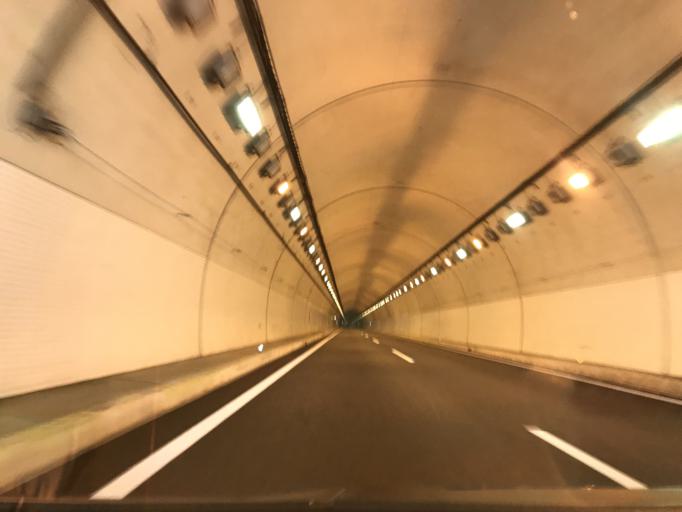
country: JP
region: Fukuoka
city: Kitakyushu
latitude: 33.8133
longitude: 130.9073
